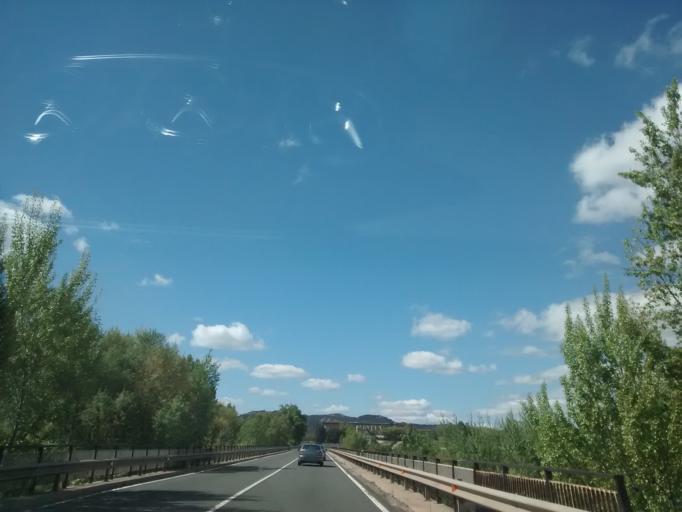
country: ES
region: La Rioja
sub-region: Provincia de La Rioja
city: Haro
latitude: 42.5807
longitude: -2.8441
